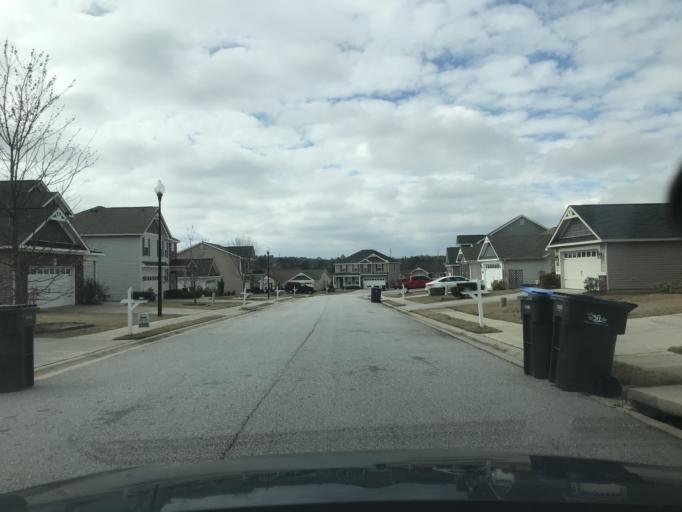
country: US
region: Georgia
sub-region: Columbia County
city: Grovetown
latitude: 33.4396
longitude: -82.1482
